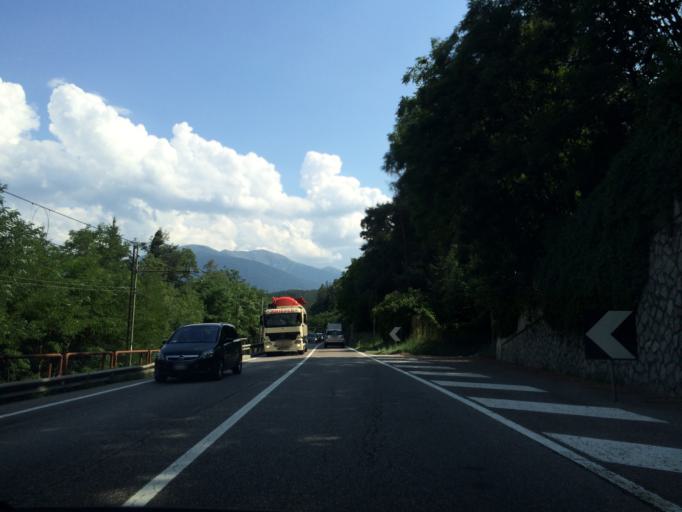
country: IT
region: Trentino-Alto Adige
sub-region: Bolzano
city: Rio di Pusteria
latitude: 46.7885
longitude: 11.6660
